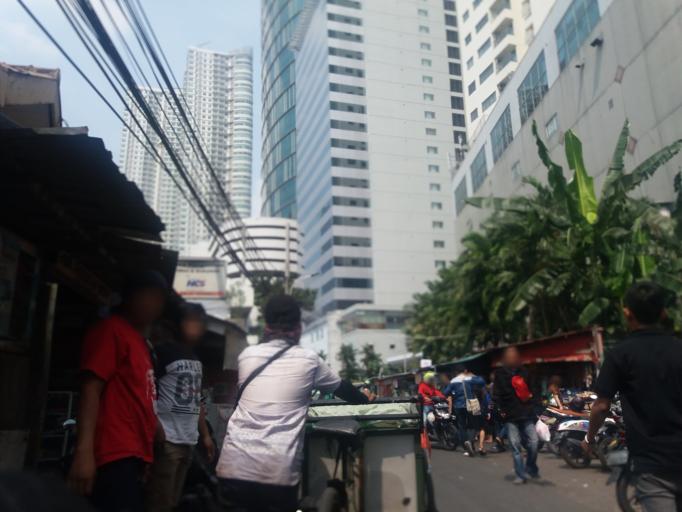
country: ID
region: Jakarta Raya
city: Jakarta
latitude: -6.2235
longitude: 106.8271
